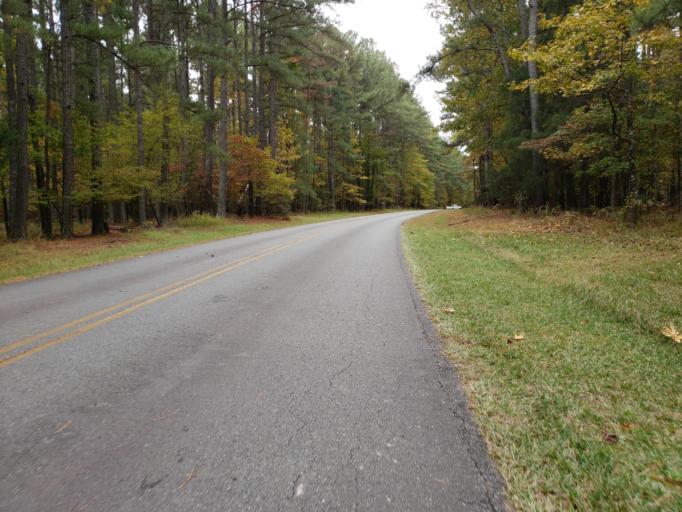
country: US
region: North Carolina
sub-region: Chatham County
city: Fearrington Village
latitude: 35.7589
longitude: -79.0442
